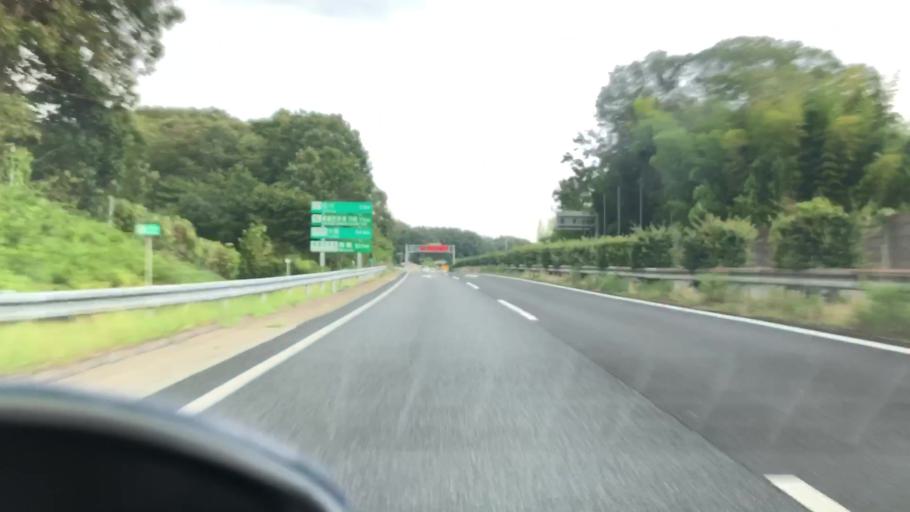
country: JP
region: Hyogo
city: Yashiro
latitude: 34.8928
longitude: 135.0860
